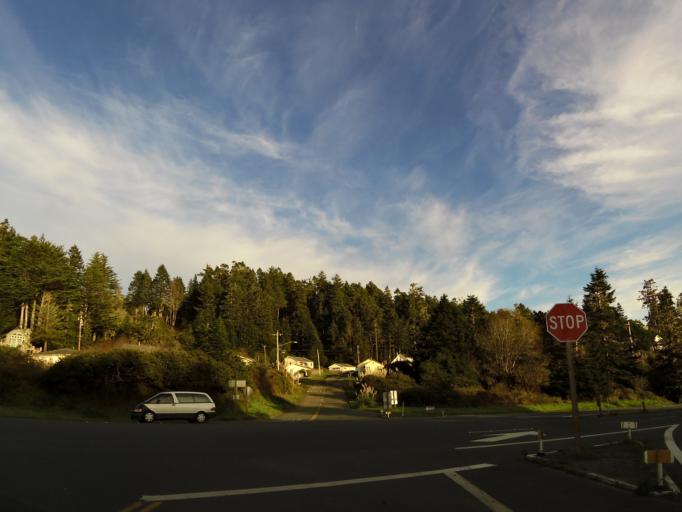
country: US
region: California
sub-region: Mendocino County
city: Fort Bragg
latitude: 39.3066
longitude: -123.7938
